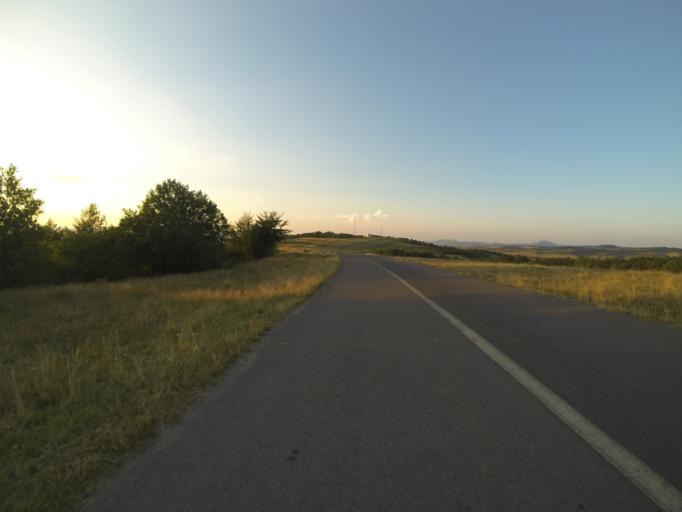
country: RO
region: Brasov
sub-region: Comuna Sinca Veche
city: Sinca Veche
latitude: 45.7481
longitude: 25.1676
